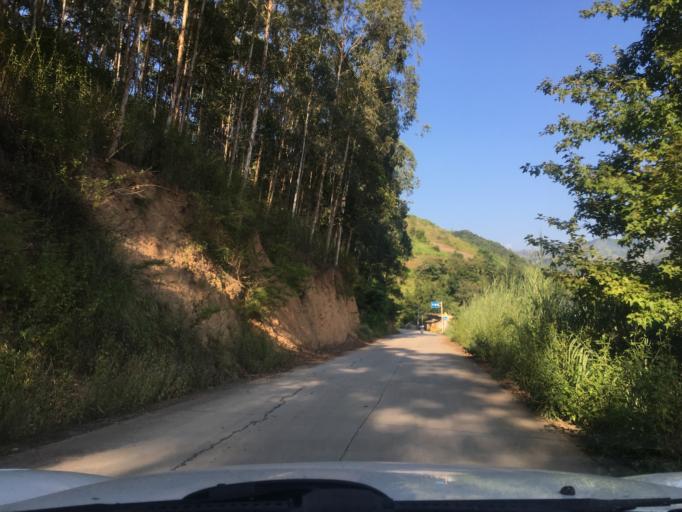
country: CN
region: Guangxi Zhuangzu Zizhiqu
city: Xinzhou
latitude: 25.3906
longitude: 105.7675
